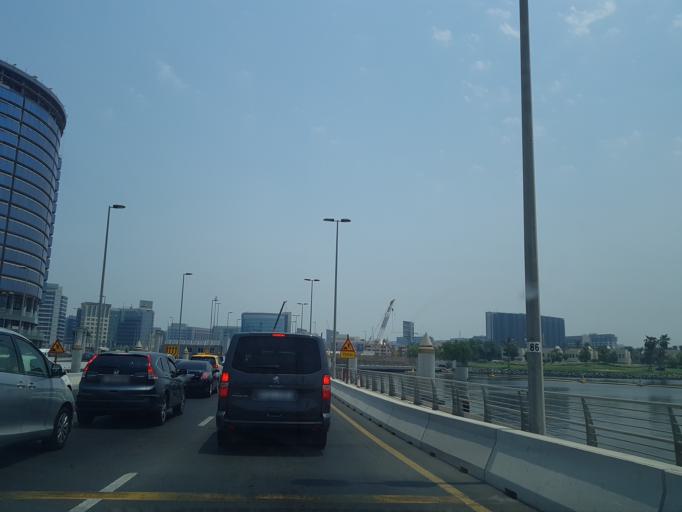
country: AE
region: Ash Shariqah
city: Sharjah
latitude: 25.2490
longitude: 55.3263
